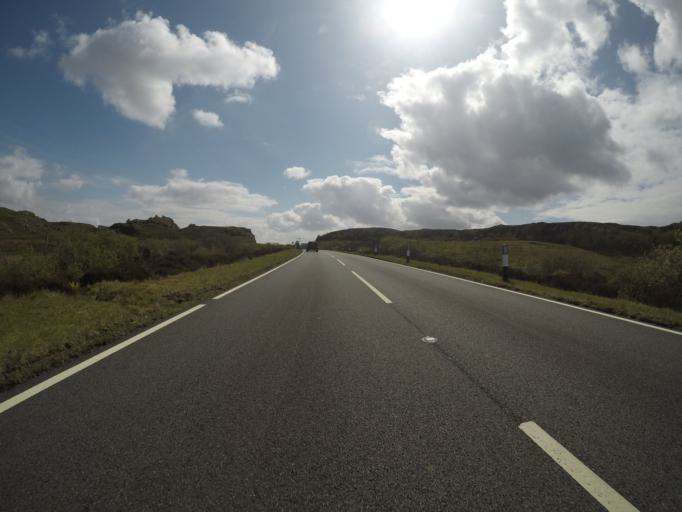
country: GB
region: Scotland
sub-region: Highland
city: Portree
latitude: 57.5172
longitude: -6.3420
